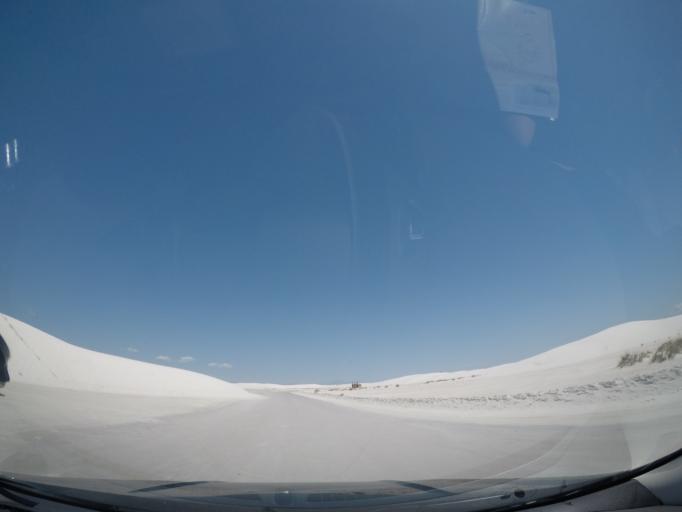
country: US
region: New Mexico
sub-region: Otero County
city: Holloman Air Force Base
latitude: 32.8114
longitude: -106.2625
